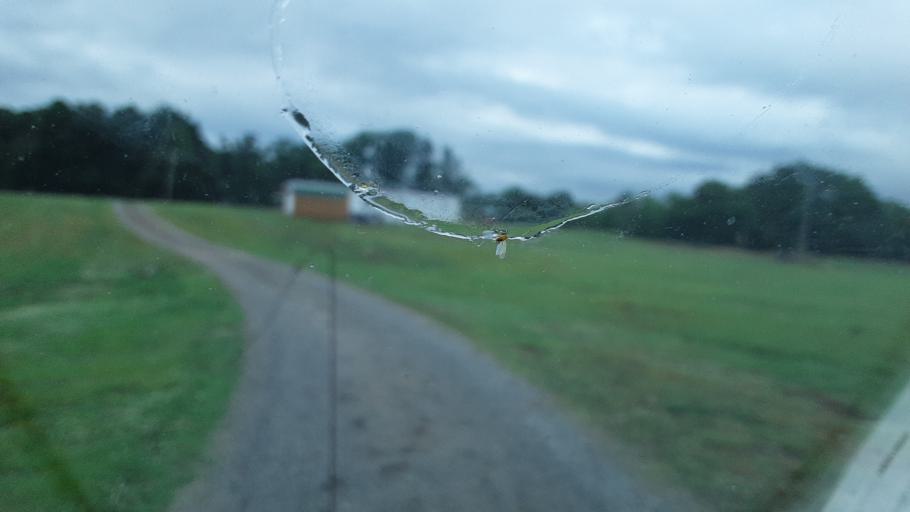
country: US
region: North Carolina
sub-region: Yadkin County
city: Yadkinville
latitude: 36.0516
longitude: -80.8251
